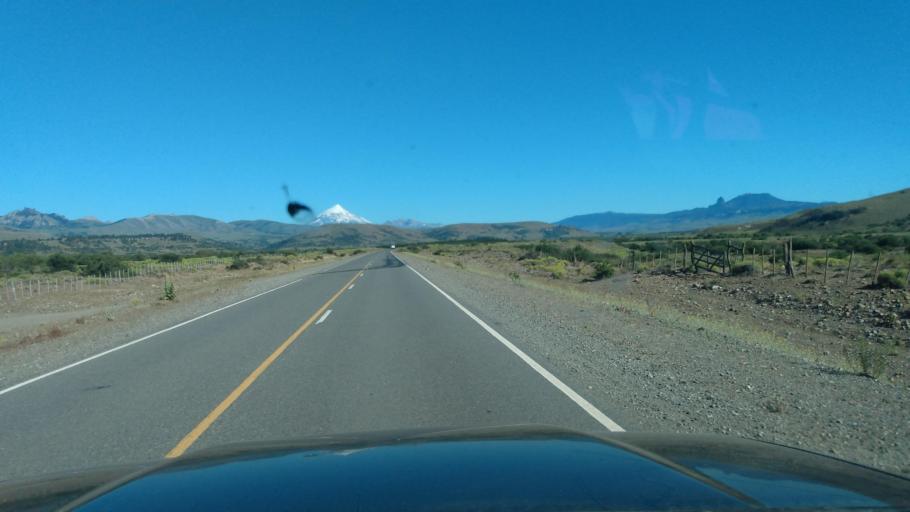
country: AR
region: Neuquen
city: Junin de los Andes
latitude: -39.8833
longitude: -71.1606
